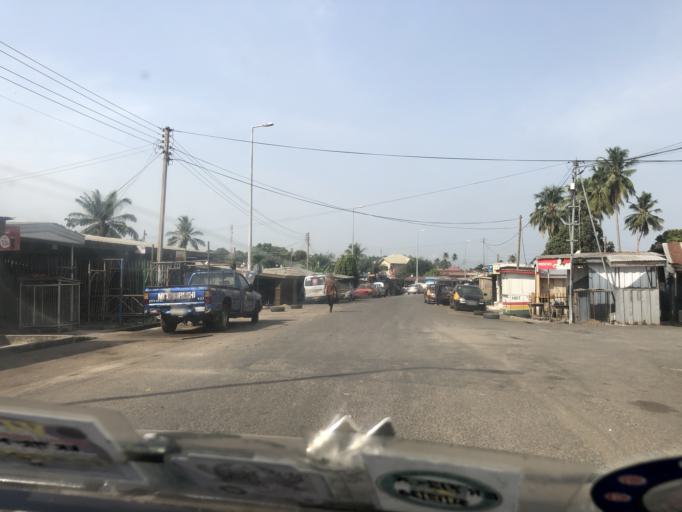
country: GH
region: Eastern
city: Koforidua
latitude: 6.0936
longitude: -0.2628
